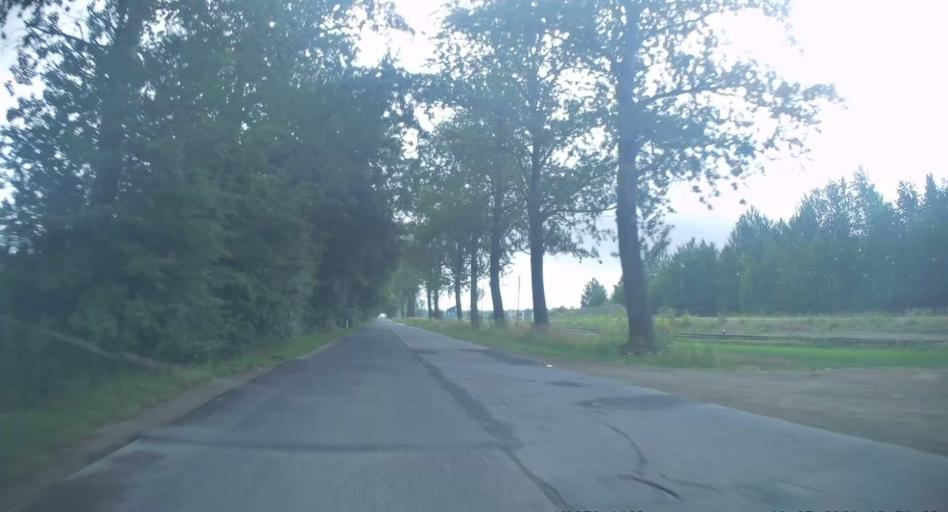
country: PL
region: Opole Voivodeship
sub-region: Powiat nyski
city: Paczkow
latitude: 50.4829
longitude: 16.9902
